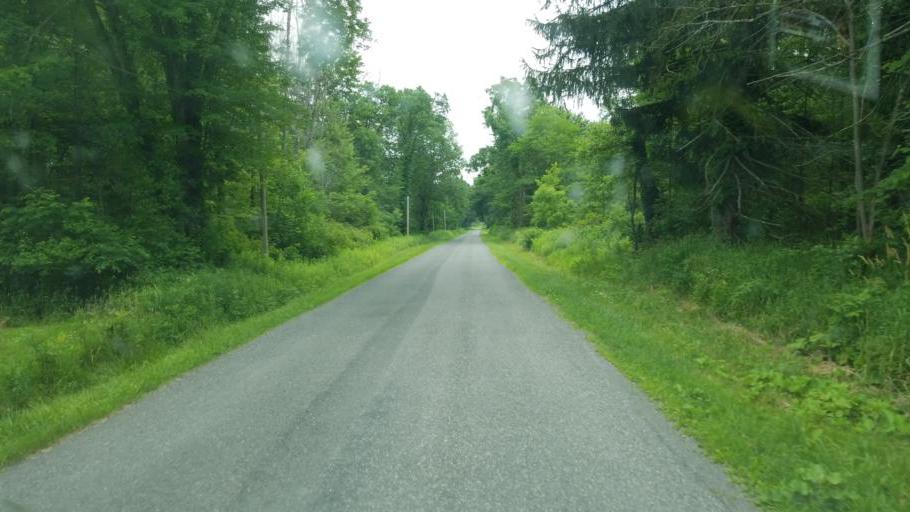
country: US
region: Ohio
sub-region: Trumbull County
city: Cortland
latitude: 41.4538
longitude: -80.7624
